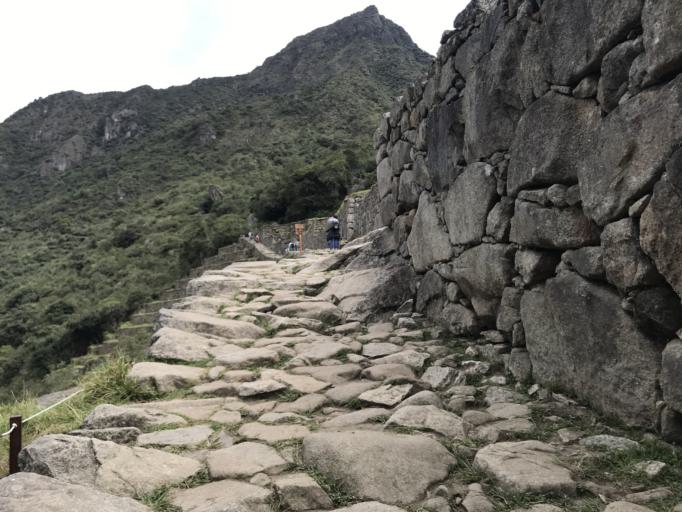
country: PE
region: Cusco
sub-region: Provincia de La Convencion
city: Santa Teresa
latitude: -13.1662
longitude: -72.5440
